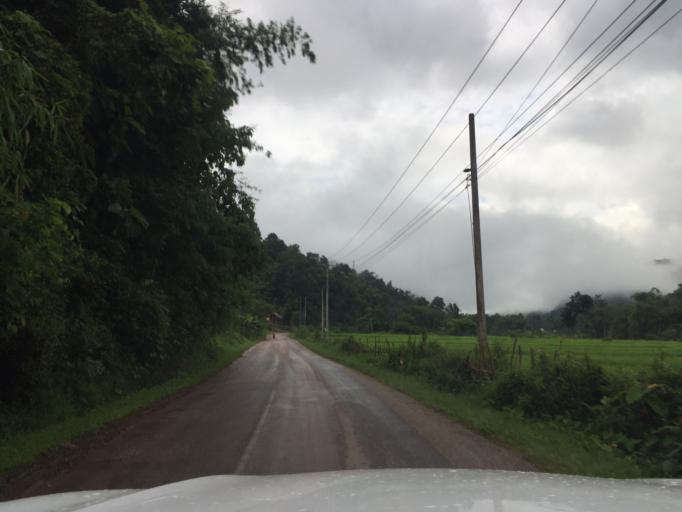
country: LA
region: Oudomxai
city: Muang La
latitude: 20.8451
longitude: 102.1048
